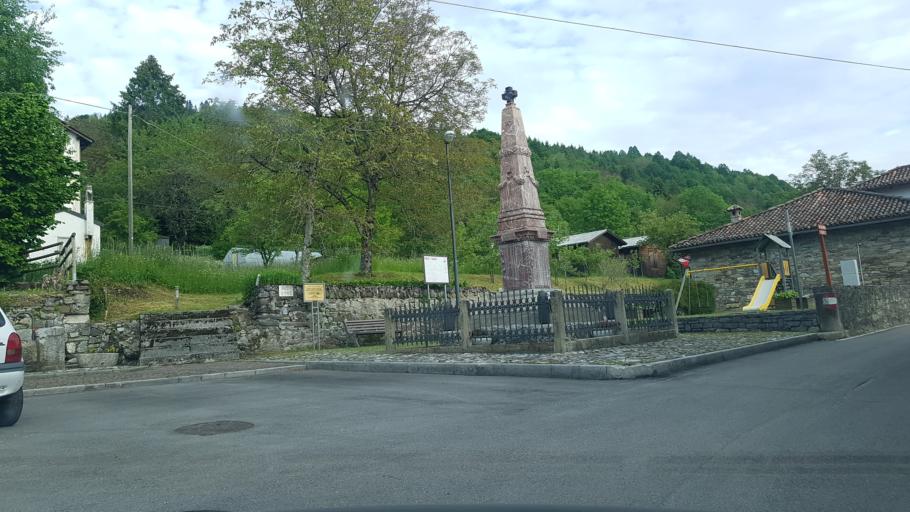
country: IT
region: Friuli Venezia Giulia
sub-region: Provincia di Udine
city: Arta Terme
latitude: 46.4708
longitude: 13.0067
